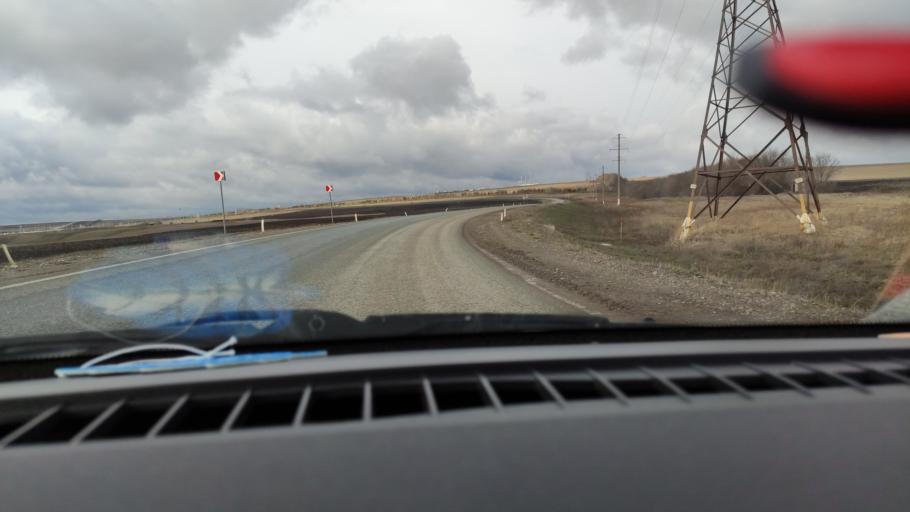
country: RU
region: Tatarstan
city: Cheremshan
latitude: 54.8591
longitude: 51.5886
